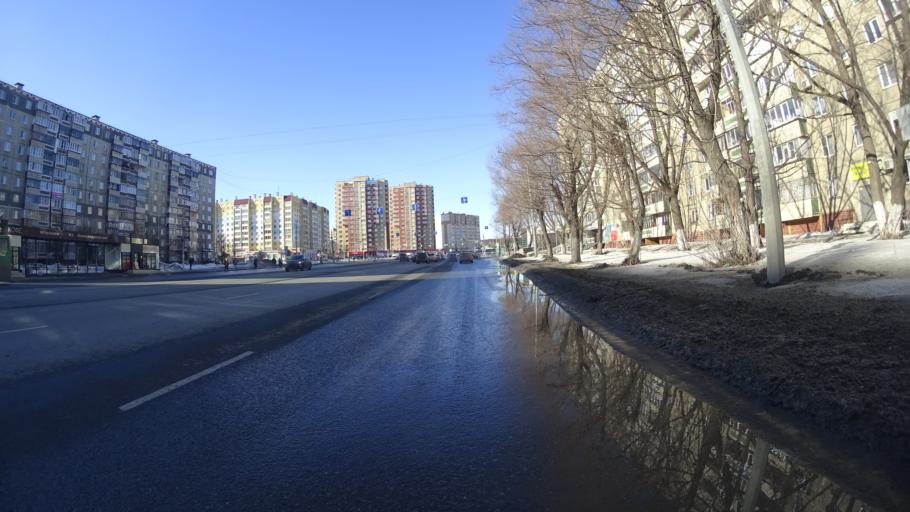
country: RU
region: Chelyabinsk
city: Roshchino
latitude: 55.1901
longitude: 61.2823
